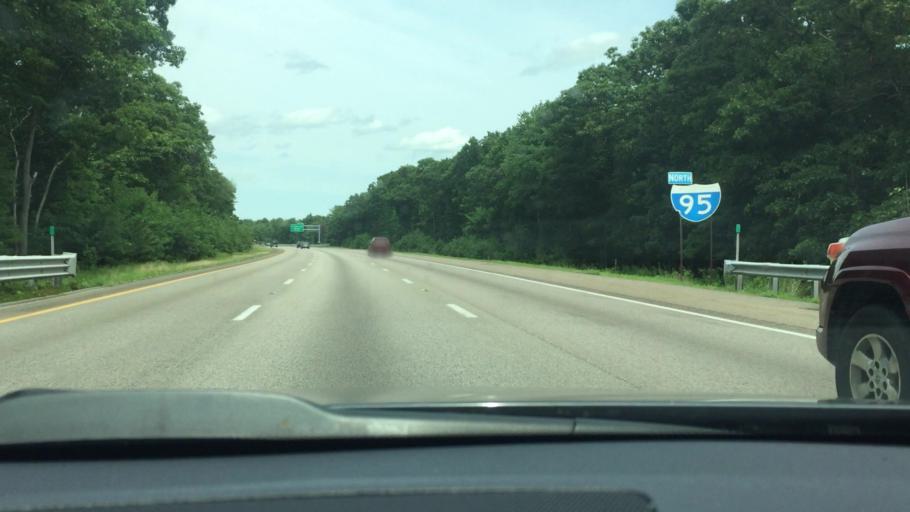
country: US
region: Massachusetts
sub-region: Norfolk County
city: Foxborough
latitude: 42.0787
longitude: -71.2224
